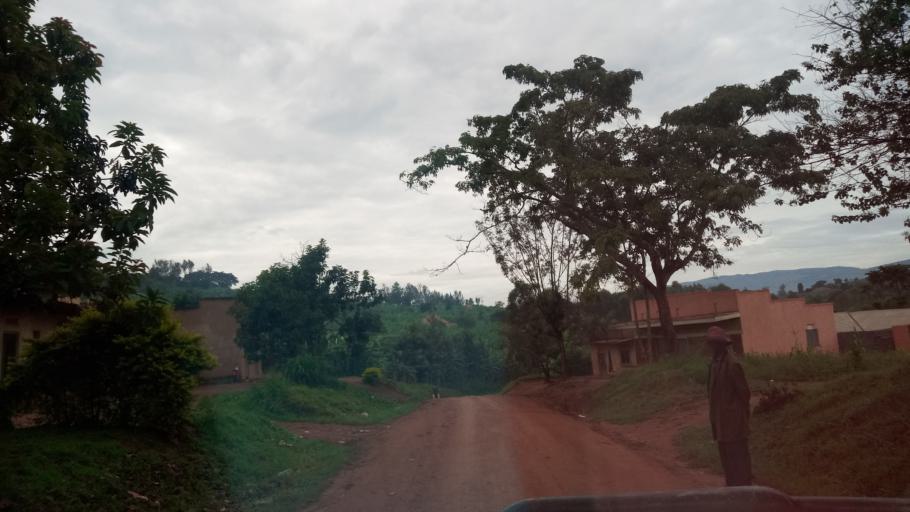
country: UG
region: Western Region
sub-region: Buhweju District
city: Buhweju
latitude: -0.1714
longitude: 30.4613
